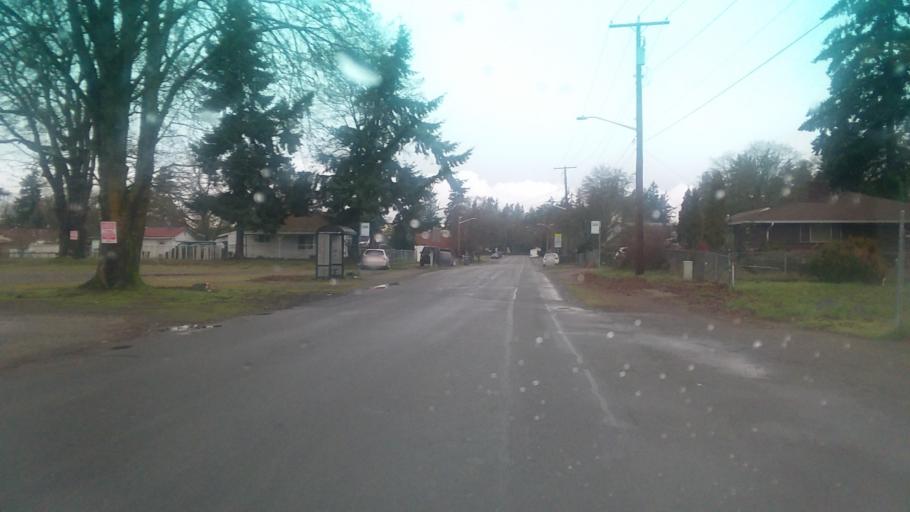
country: US
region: Washington
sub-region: Pierce County
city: Fort Lewis
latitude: 47.1236
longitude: -122.5509
